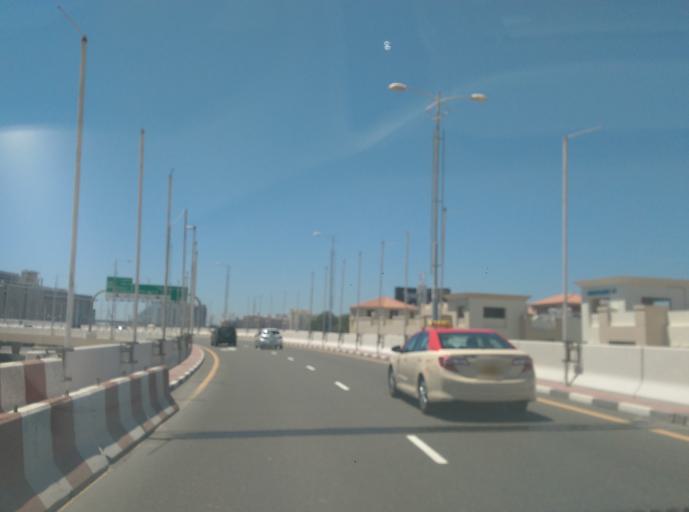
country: AE
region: Dubai
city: Dubai
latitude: 25.1005
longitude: 55.1613
